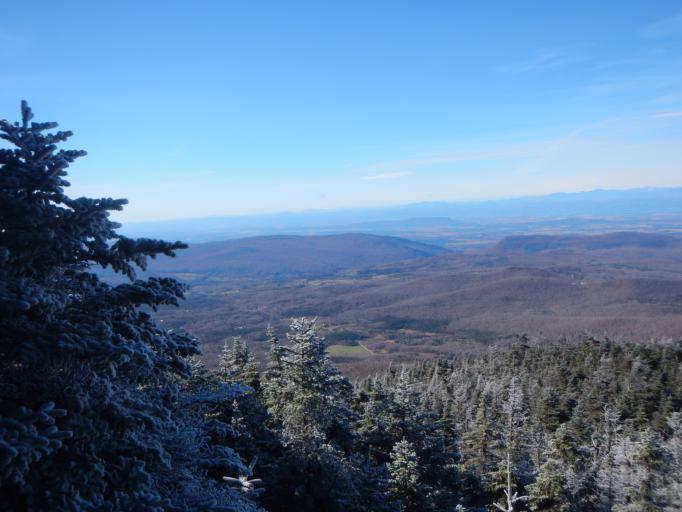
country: US
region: Vermont
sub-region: Addison County
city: Bristol
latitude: 44.1605
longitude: -72.9294
